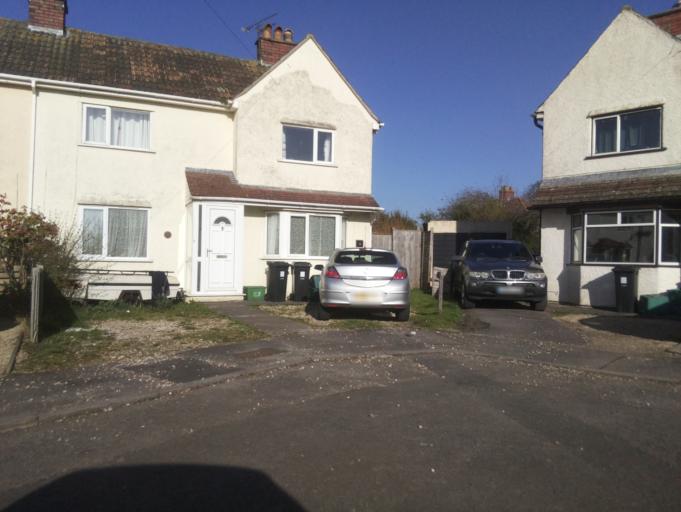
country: GB
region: England
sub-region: South Gloucestershire
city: Yate
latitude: 51.5382
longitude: -2.4251
